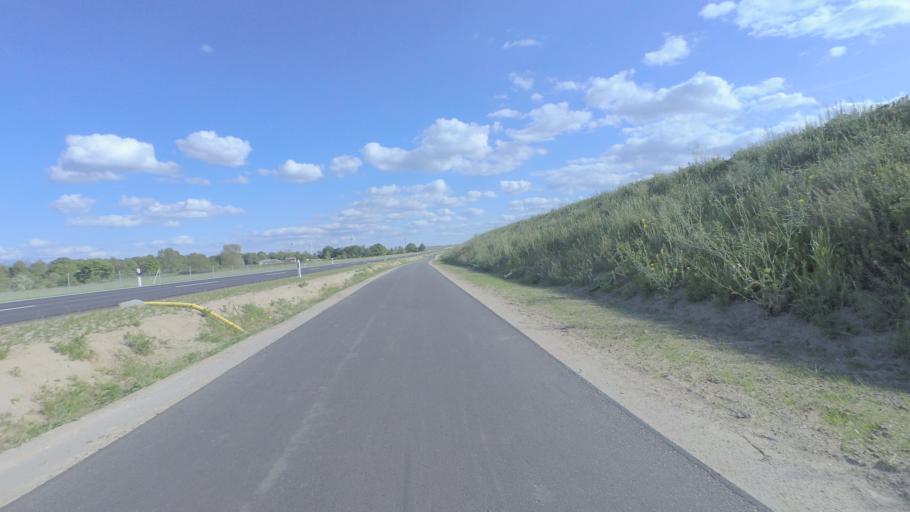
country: DE
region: Brandenburg
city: Stahnsdorf
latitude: 52.3768
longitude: 13.2362
